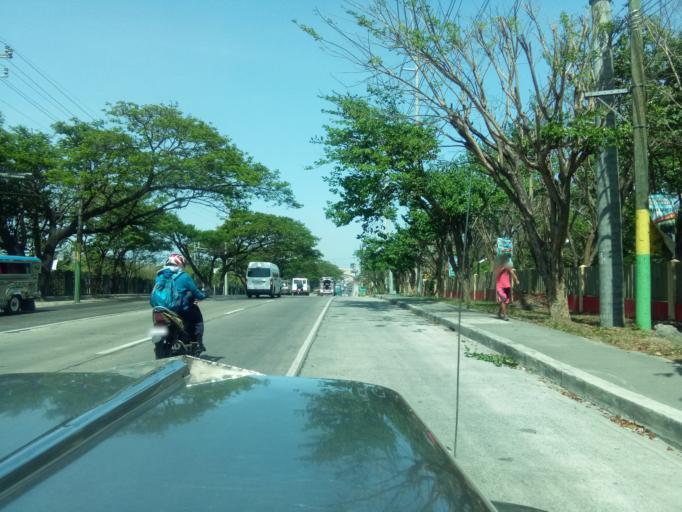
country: PH
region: Calabarzon
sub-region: Province of Cavite
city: Dasmarinas
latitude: 14.2966
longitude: 120.9459
